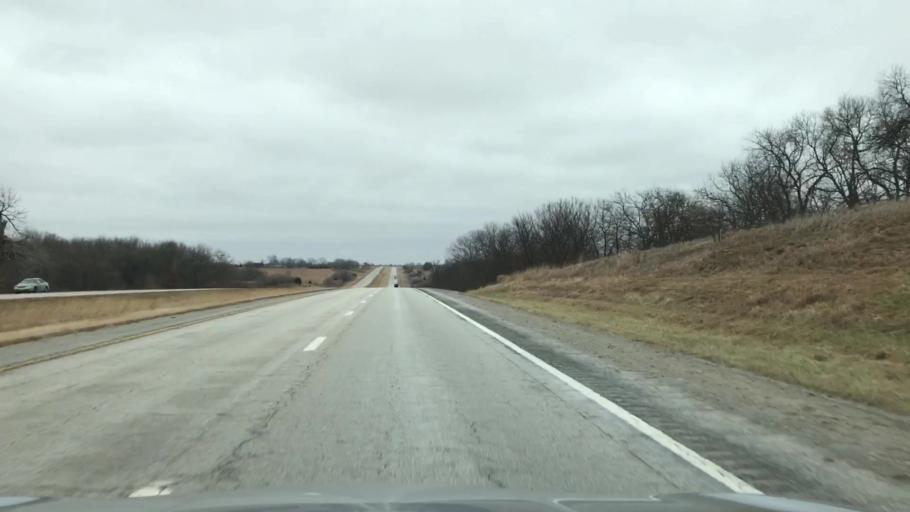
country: US
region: Missouri
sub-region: Caldwell County
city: Hamilton
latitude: 39.7500
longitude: -94.1059
